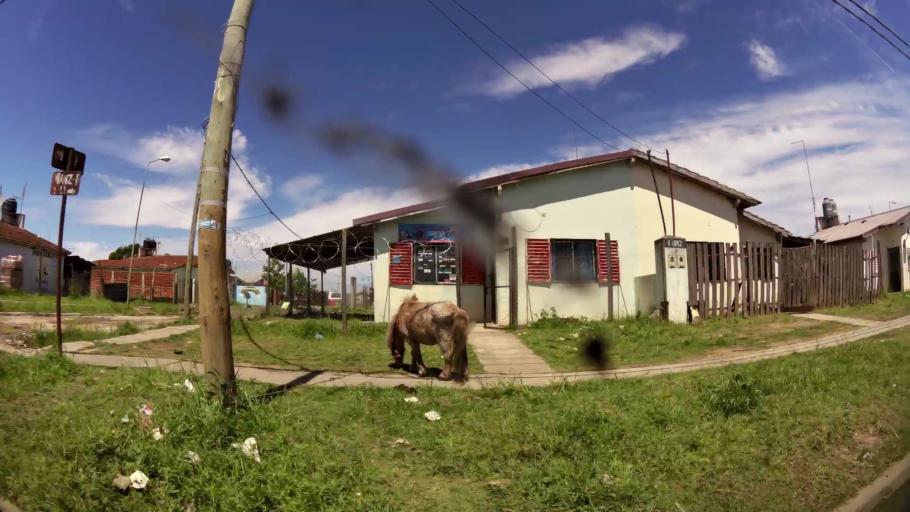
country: AR
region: Buenos Aires
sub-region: Partido de Quilmes
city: Quilmes
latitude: -34.7428
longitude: -58.3100
